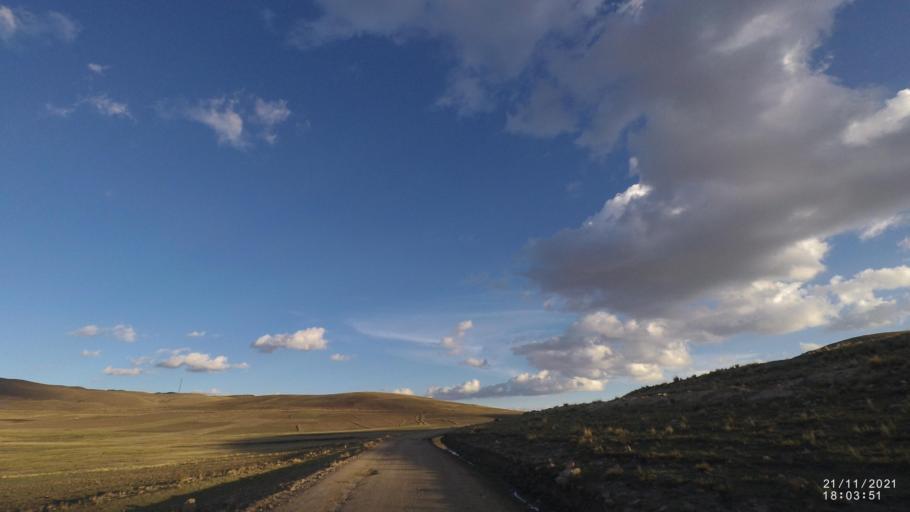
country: BO
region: Cochabamba
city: Cochabamba
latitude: -17.2633
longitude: -66.2230
